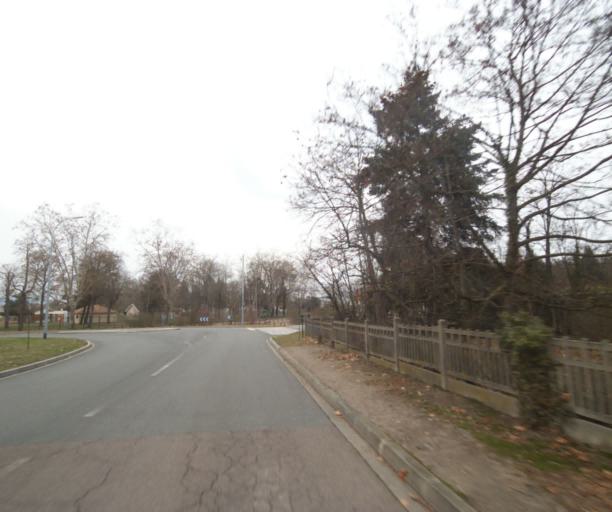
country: FR
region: Rhone-Alpes
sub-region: Departement de la Loire
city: Le Coteau
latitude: 46.0560
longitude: 4.0959
